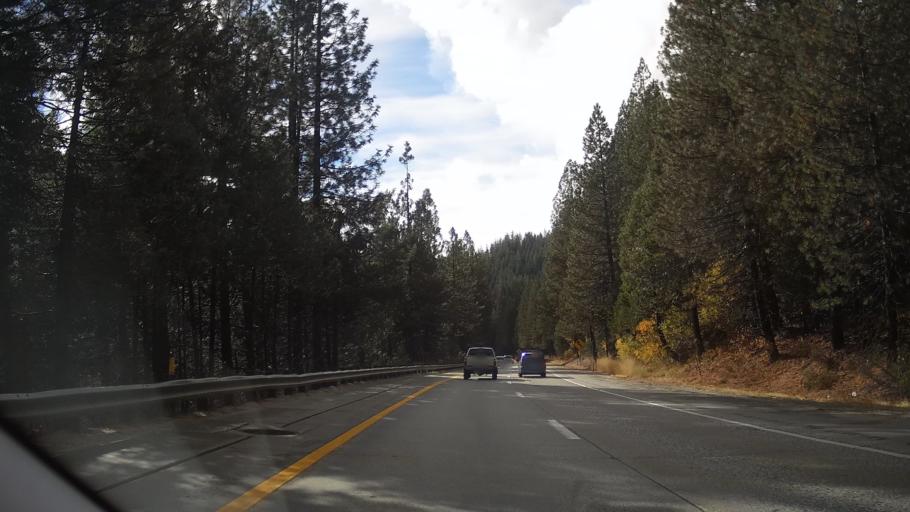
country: US
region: California
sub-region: Placer County
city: Foresthill
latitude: 39.2448
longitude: -120.7474
